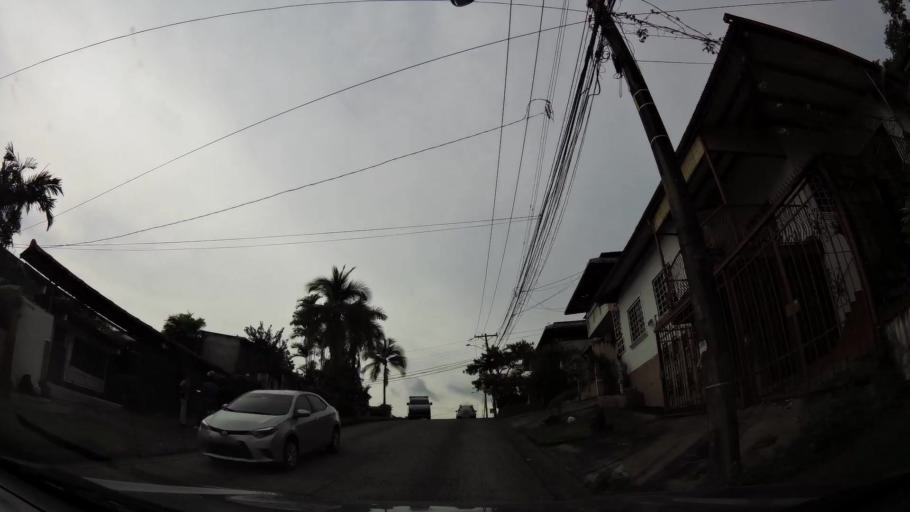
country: PA
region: Panama
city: Panama
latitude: 9.0097
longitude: -79.5291
